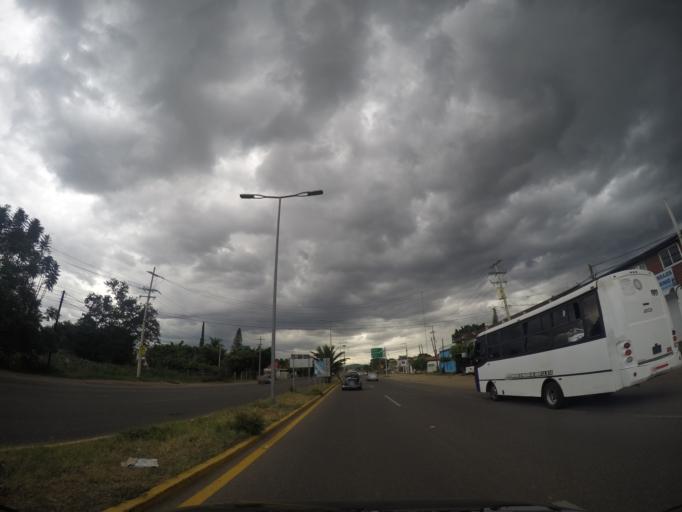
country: MX
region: Oaxaca
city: Tlalixtac de Cabrera
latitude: 17.0587
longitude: -96.6594
